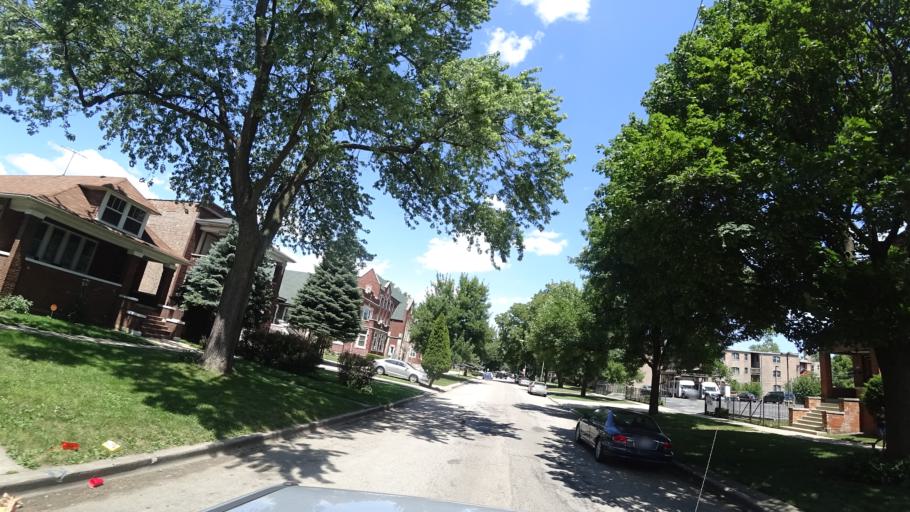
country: US
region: Illinois
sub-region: Cook County
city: Chicago
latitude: 41.7664
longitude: -87.6217
